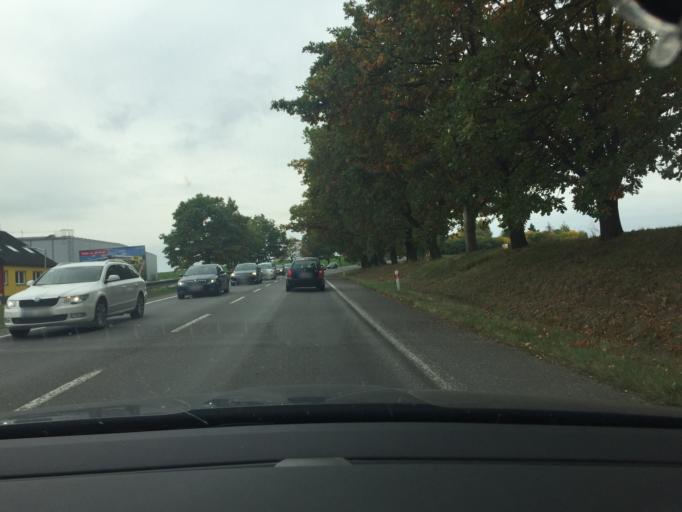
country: CZ
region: Jihocesky
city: Cimelice
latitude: 49.4613
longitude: 14.0681
